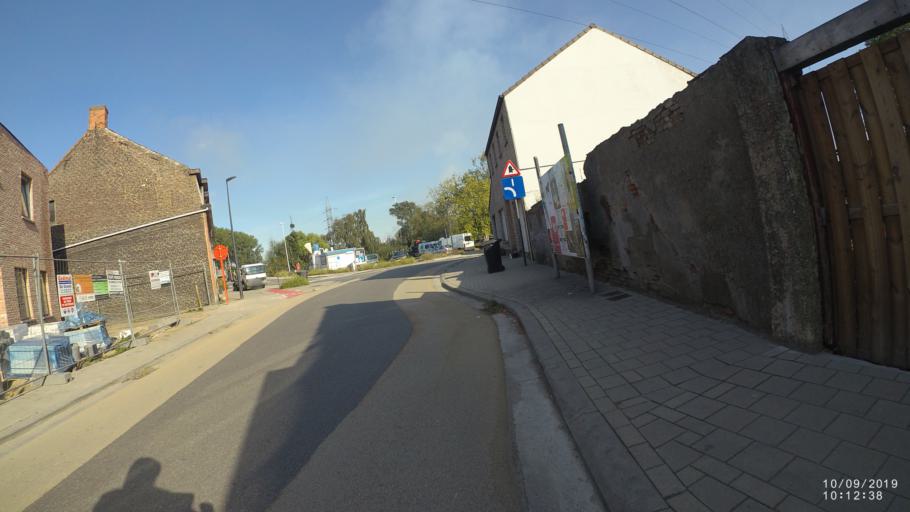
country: BE
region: Flanders
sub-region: Provincie Oost-Vlaanderen
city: Zelzate
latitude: 51.1561
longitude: 3.8156
